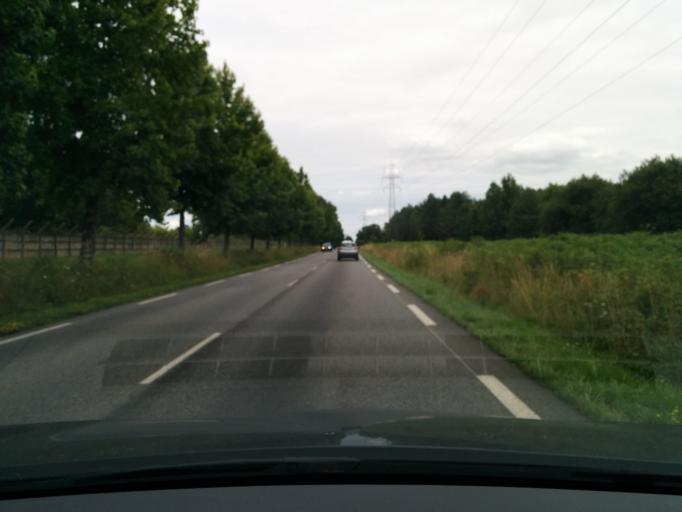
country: FR
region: Midi-Pyrenees
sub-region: Departement des Hautes-Pyrenees
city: La Barthe-de-Neste
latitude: 43.0843
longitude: 0.3661
